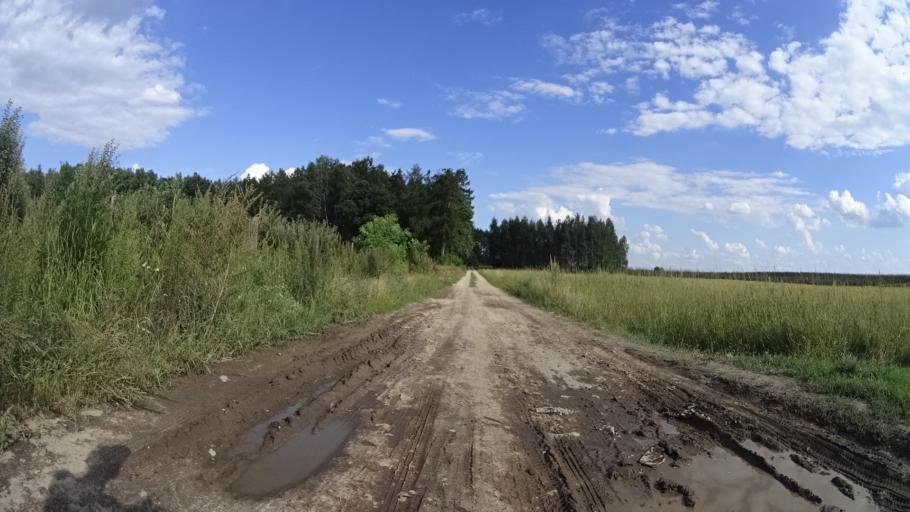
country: PL
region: Masovian Voivodeship
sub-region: Powiat grojecki
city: Mogielnica
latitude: 51.6765
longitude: 20.7797
